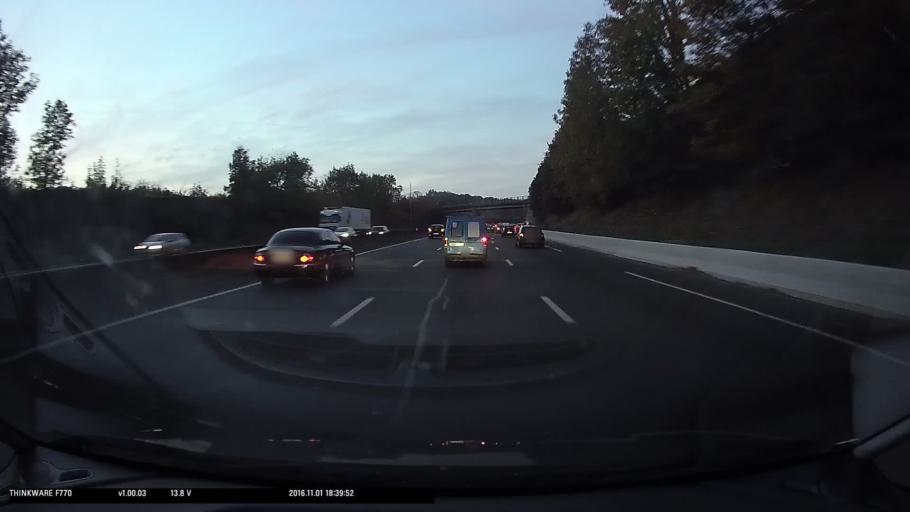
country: FR
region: Ile-de-France
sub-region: Departement de l'Essonne
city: Villemoisson-sur-Orge
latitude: 48.6804
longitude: 2.3321
